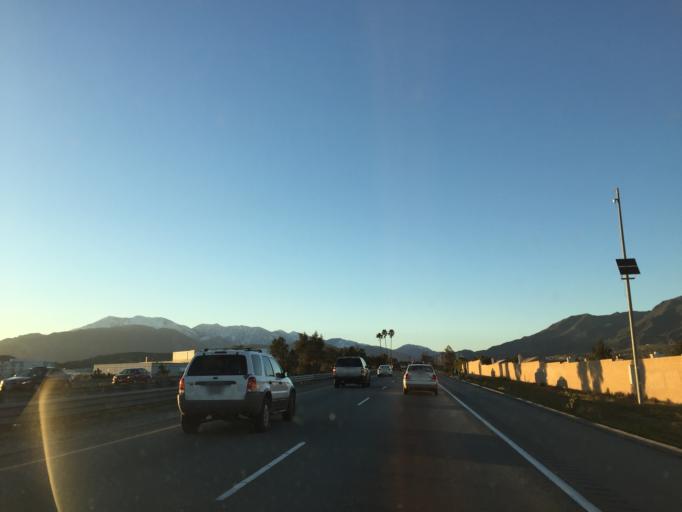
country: US
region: California
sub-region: San Bernardino County
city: Muscoy
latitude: 34.1839
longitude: -117.3509
